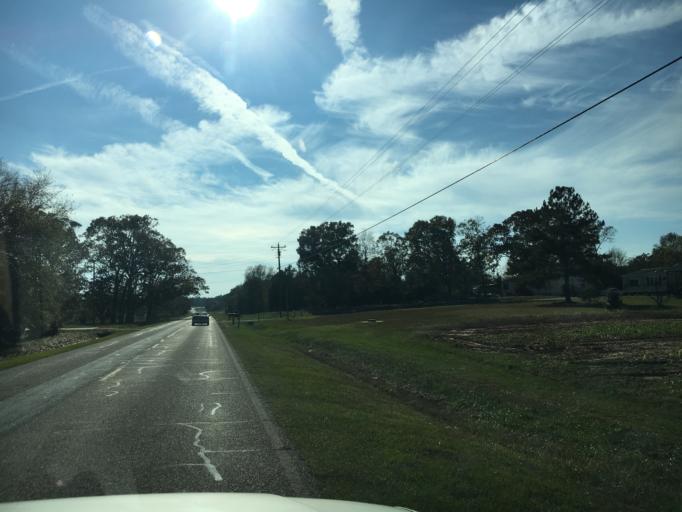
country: US
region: Georgia
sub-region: Hart County
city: Hartwell
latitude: 34.2966
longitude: -82.8389
